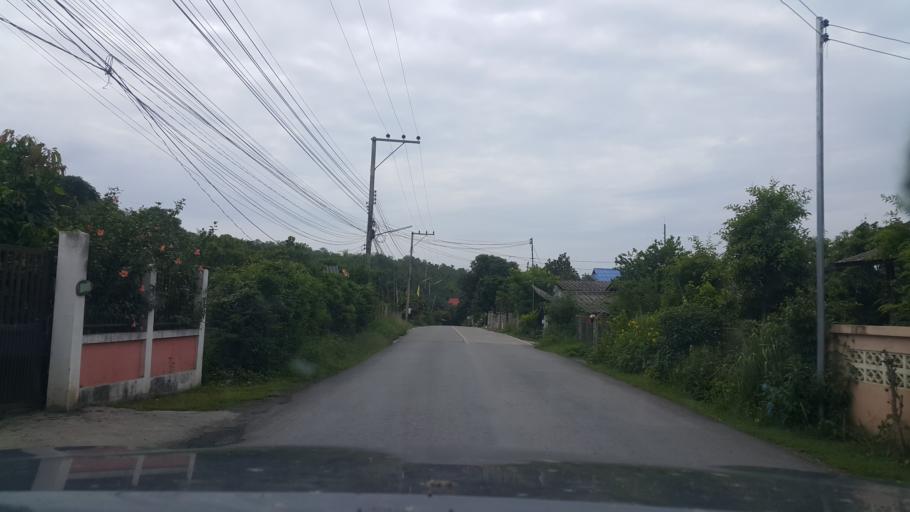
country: TH
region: Chiang Mai
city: San Pa Tong
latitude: 18.6741
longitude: 98.8300
